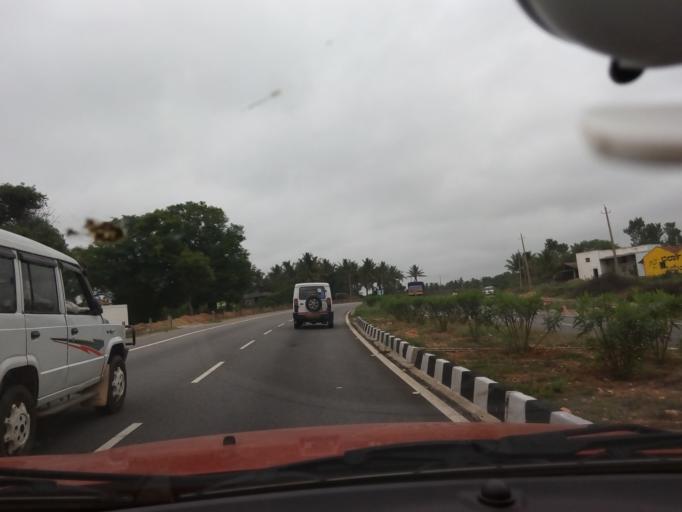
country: IN
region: Karnataka
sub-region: Hassan
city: Shravanabelagola
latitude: 12.9407
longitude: 76.5493
